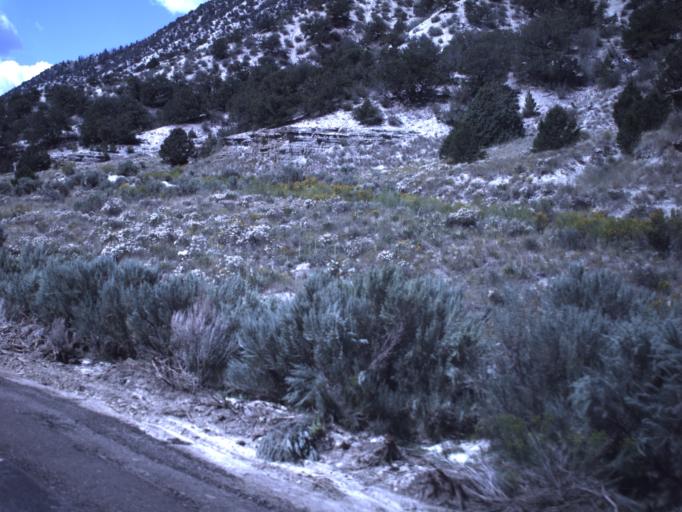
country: US
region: Utah
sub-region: Duchesne County
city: Duchesne
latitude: 39.9511
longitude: -110.6543
